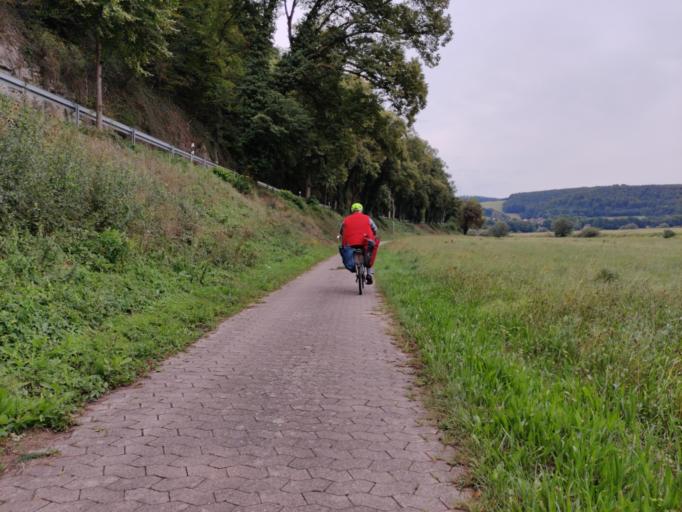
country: DE
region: Lower Saxony
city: Pegestorf
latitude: 51.9110
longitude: 9.4681
